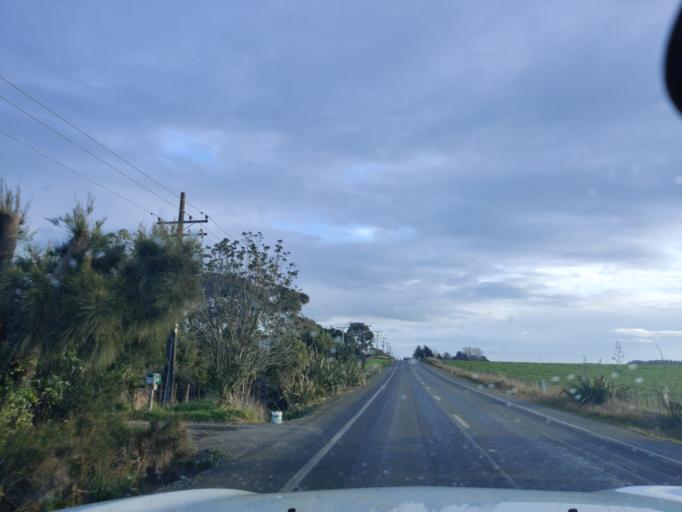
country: NZ
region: Manawatu-Wanganui
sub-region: Palmerston North City
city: Palmerston North
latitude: -40.3967
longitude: 175.6261
